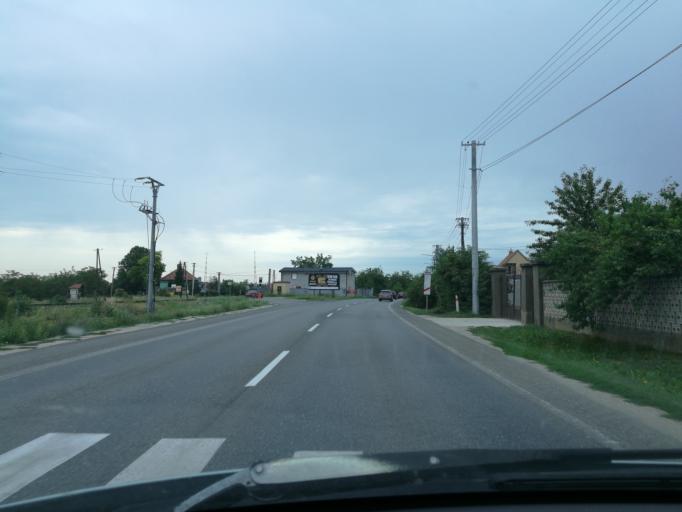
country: SK
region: Nitriansky
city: Surany
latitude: 48.1619
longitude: 18.1597
